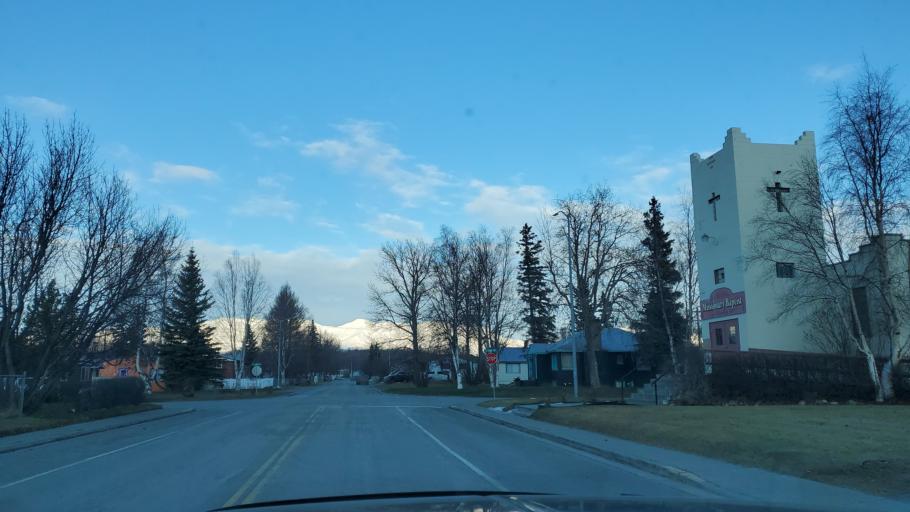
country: US
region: Alaska
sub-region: Matanuska-Susitna Borough
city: Palmer
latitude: 61.6020
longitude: -149.1165
